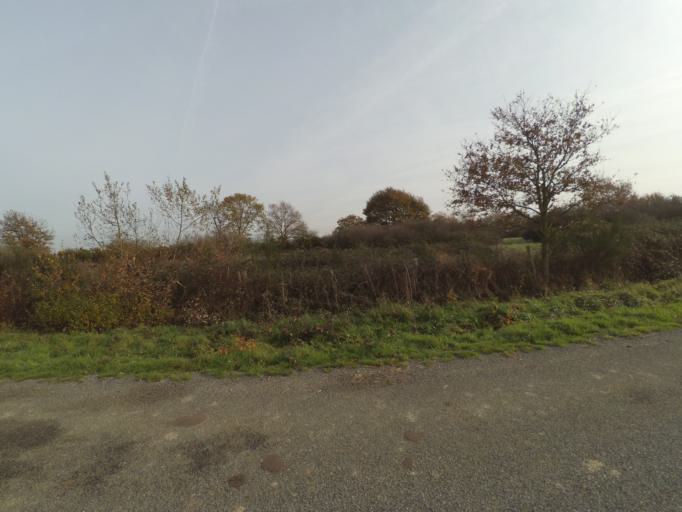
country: FR
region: Pays de la Loire
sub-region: Departement de la Loire-Atlantique
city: La Planche
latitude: 47.0111
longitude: -1.3925
